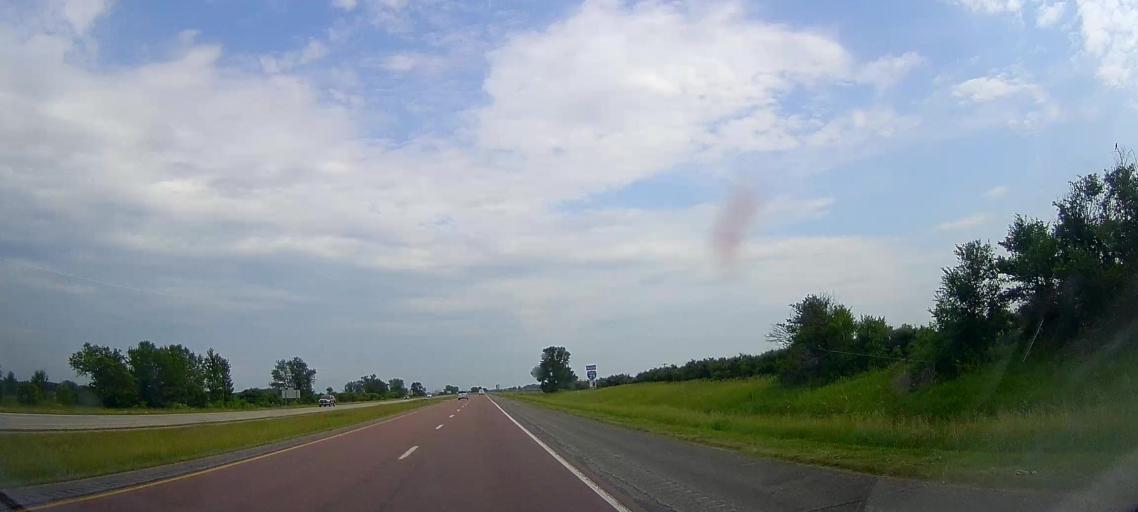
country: US
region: Iowa
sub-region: Monona County
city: Onawa
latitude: 42.0201
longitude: -96.1273
